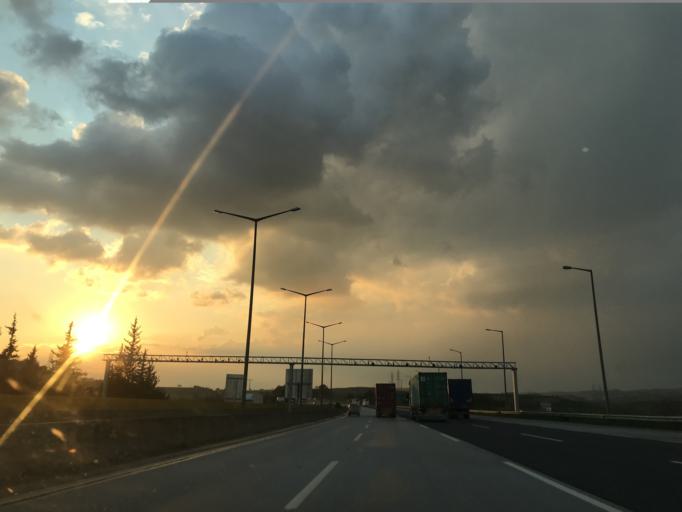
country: TR
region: Mersin
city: Yenice
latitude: 37.0395
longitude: 35.1661
